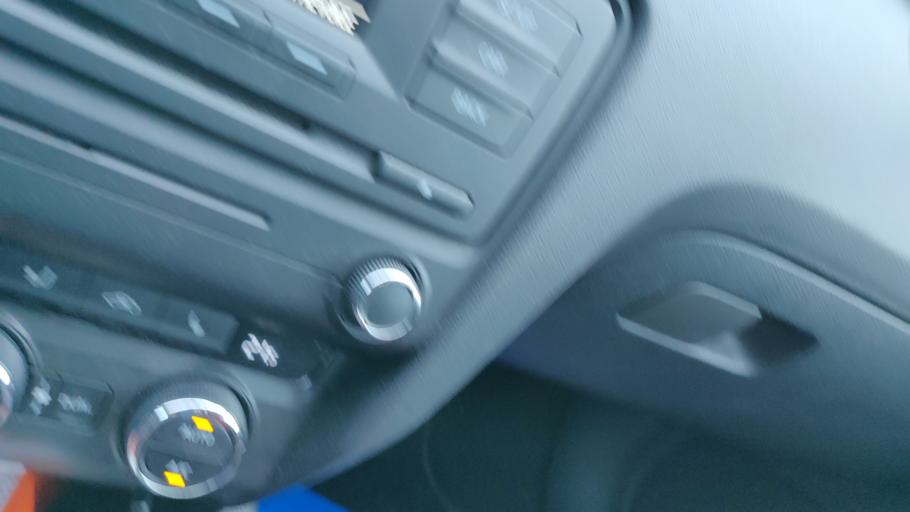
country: DK
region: North Denmark
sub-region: Alborg Kommune
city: Svenstrup
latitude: 56.9803
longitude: 9.8795
